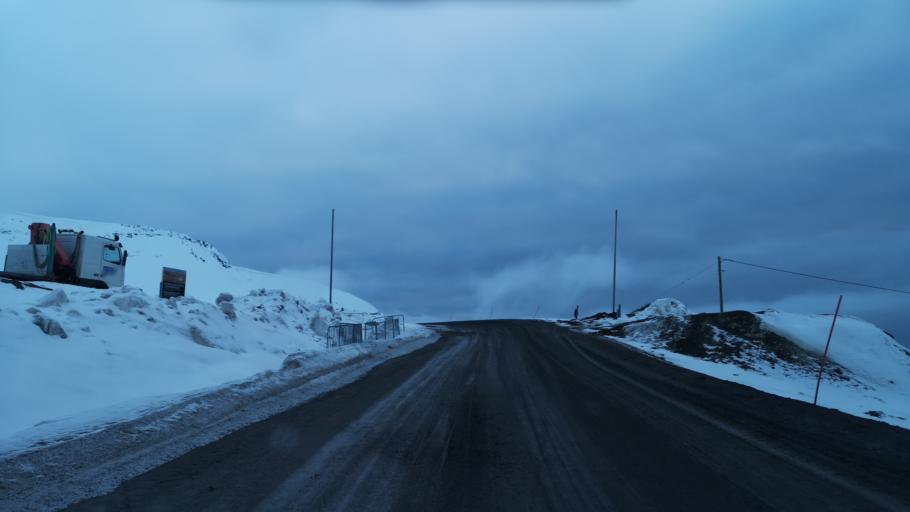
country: SJ
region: Svalbard
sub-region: Spitsbergen
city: Longyearbyen
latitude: 78.2366
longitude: 15.4858
